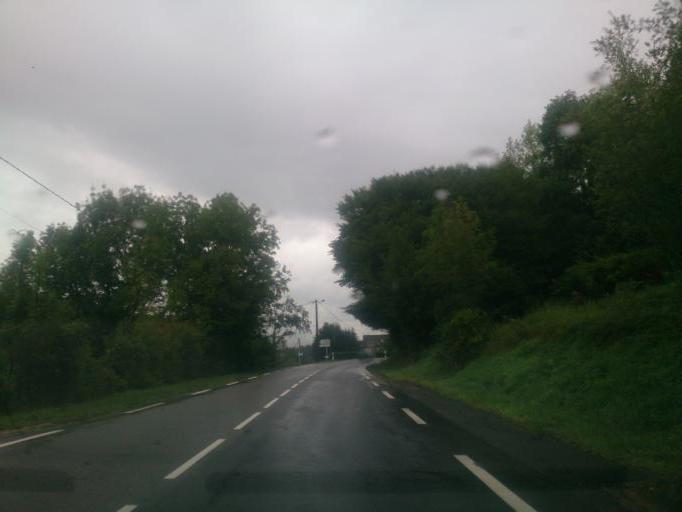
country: FR
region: Limousin
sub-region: Departement de la Correze
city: Malemort-sur-Correze
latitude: 45.1747
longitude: 1.5657
